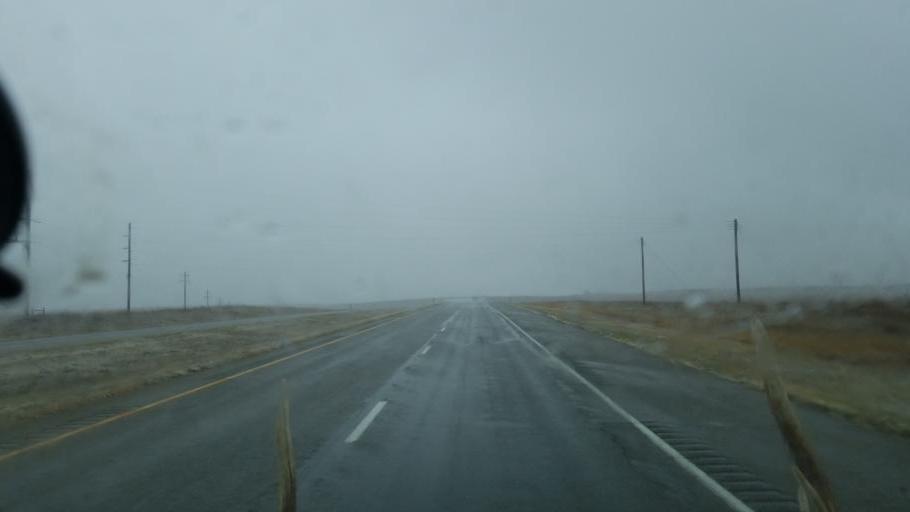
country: US
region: Colorado
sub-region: Pueblo County
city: Colorado City
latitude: 37.8859
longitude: -104.8288
